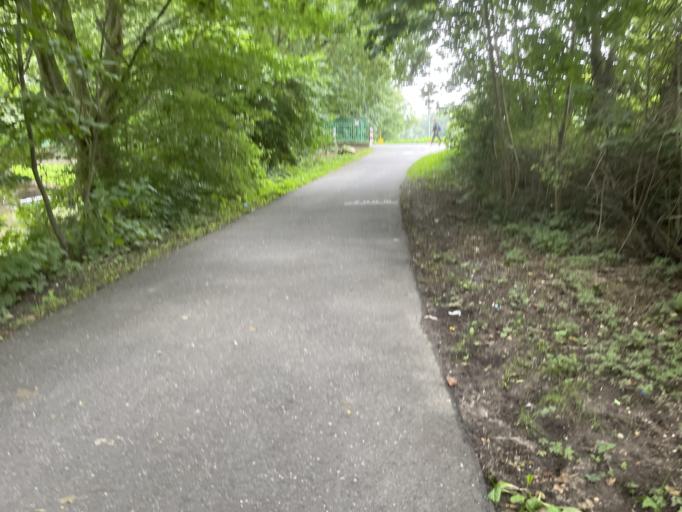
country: DE
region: North Rhine-Westphalia
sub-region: Regierungsbezirk Koln
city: Bergheim
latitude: 50.9451
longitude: 6.6381
